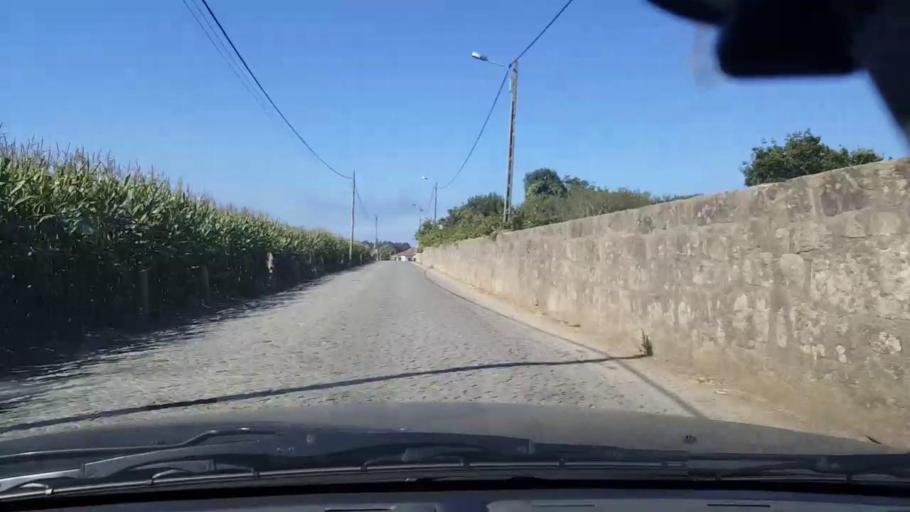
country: PT
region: Porto
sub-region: Maia
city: Gemunde
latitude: 41.2801
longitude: -8.6666
